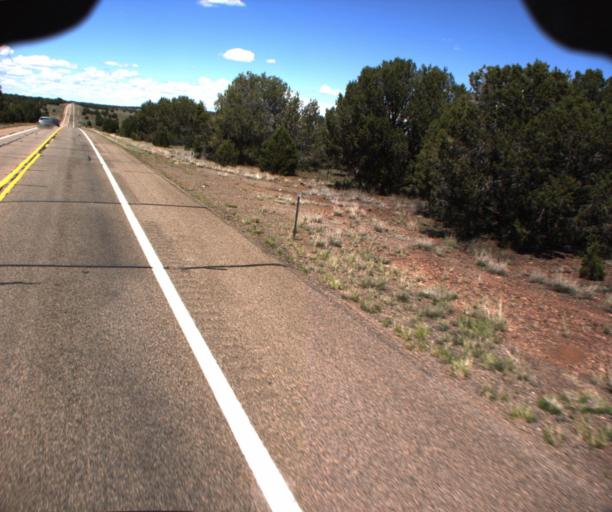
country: US
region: Arizona
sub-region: Yavapai County
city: Paulden
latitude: 35.1379
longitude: -112.4420
